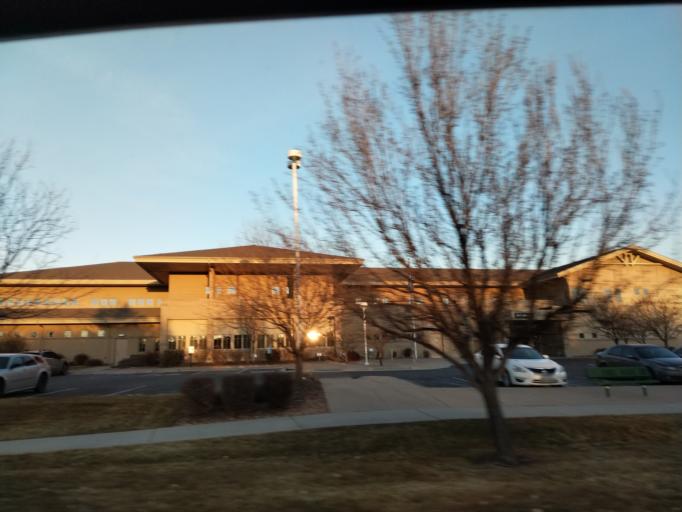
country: US
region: Colorado
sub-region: Mesa County
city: Grand Junction
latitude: 39.0965
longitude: -108.5523
